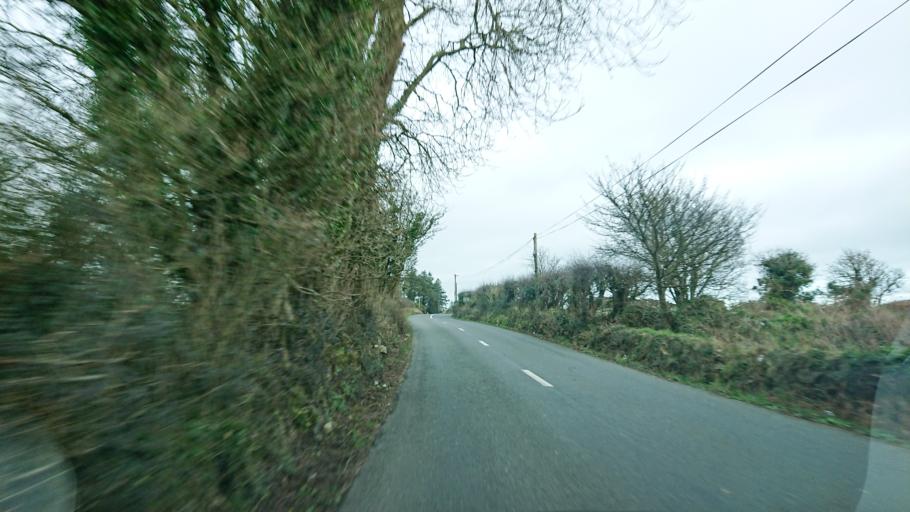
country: IE
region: Leinster
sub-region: Kilkenny
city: Mooncoin
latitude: 52.1960
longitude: -7.2717
